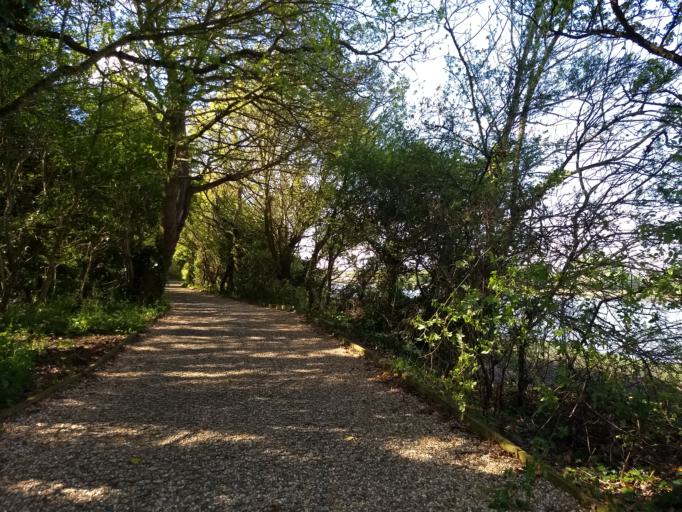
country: GB
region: England
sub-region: Isle of Wight
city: Newport
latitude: 50.7219
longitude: -1.2825
